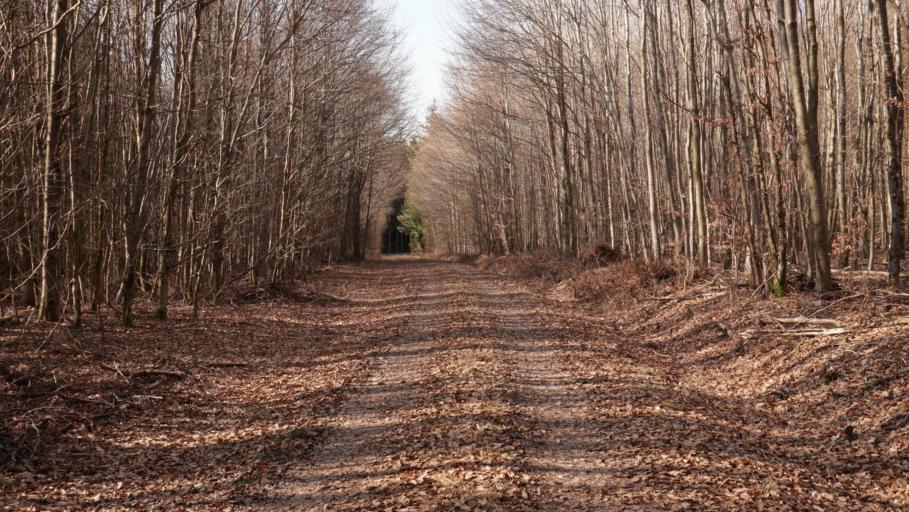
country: DE
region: Baden-Wuerttemberg
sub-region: Karlsruhe Region
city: Fahrenbach
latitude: 49.4540
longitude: 9.1332
